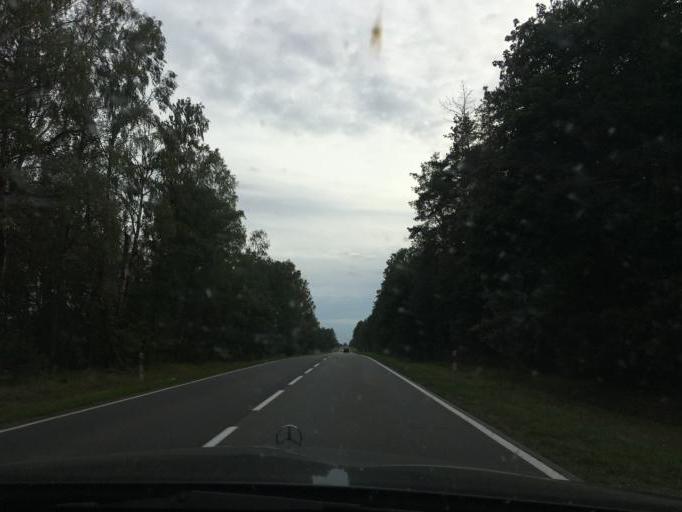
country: PL
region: Masovian Voivodeship
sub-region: Powiat ostrowski
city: Ostrow Mazowiecka
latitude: 52.8976
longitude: 21.8694
